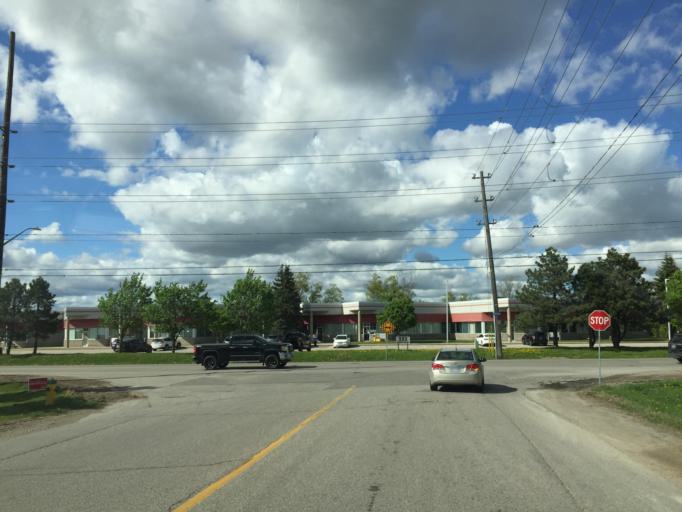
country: CA
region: Ontario
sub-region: Wellington County
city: Guelph
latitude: 43.4924
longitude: -80.2001
